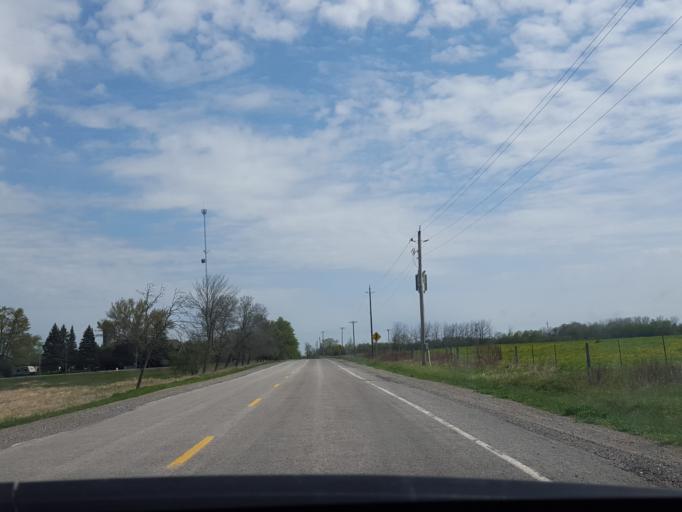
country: CA
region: Ontario
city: Uxbridge
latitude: 44.1988
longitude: -78.8775
